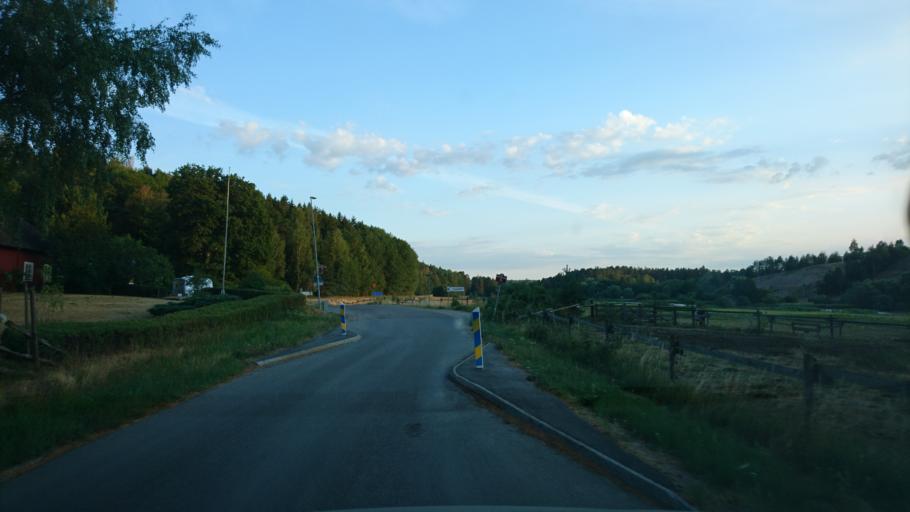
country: SE
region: Uppsala
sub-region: Uppsala Kommun
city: Saevja
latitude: 59.7957
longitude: 17.6705
